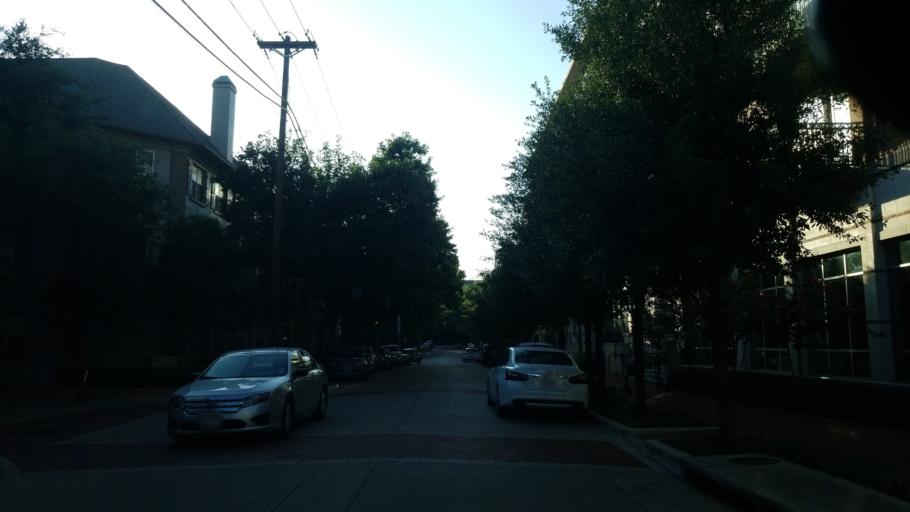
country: US
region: Texas
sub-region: Dallas County
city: Dallas
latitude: 32.7943
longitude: -96.7970
